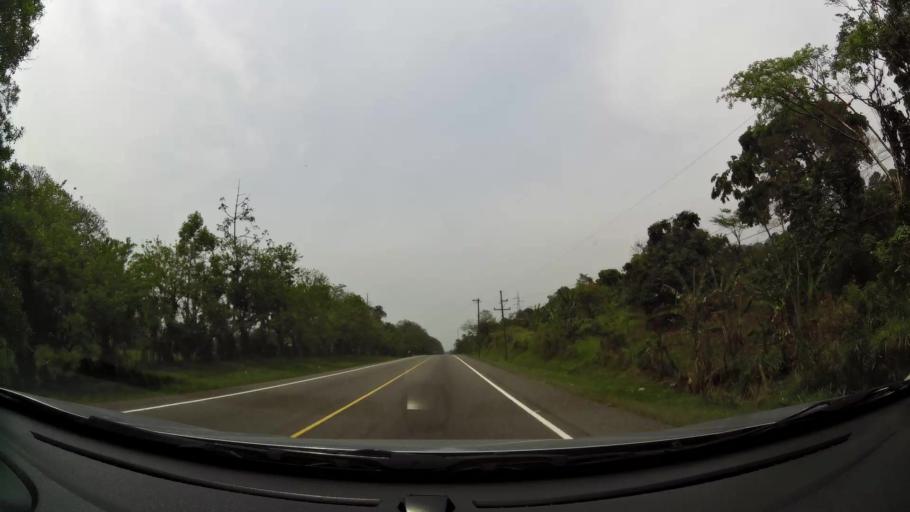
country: HN
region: Cortes
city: La Guama
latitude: 14.8327
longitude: -87.9603
